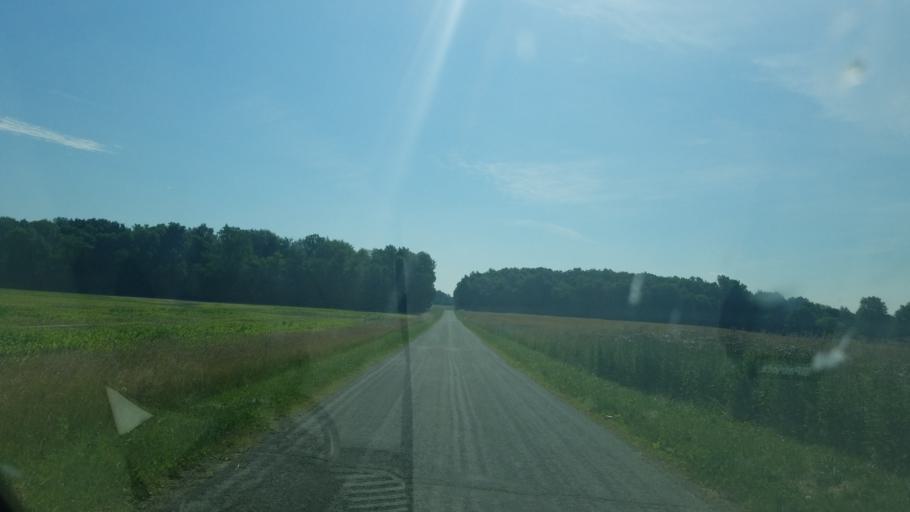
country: US
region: Ohio
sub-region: Wyandot County
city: Carey
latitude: 40.9782
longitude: -83.2767
